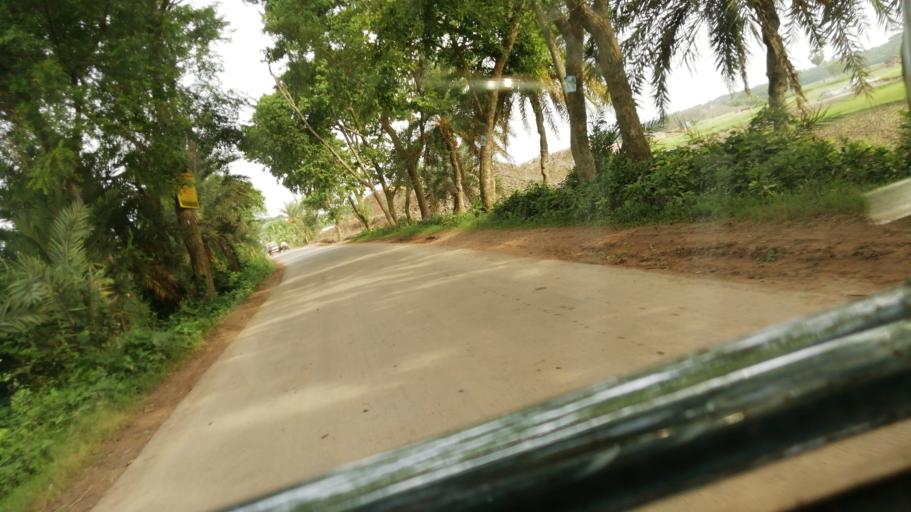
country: BD
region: Khulna
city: Kesabpur
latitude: 23.0265
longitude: 89.2517
